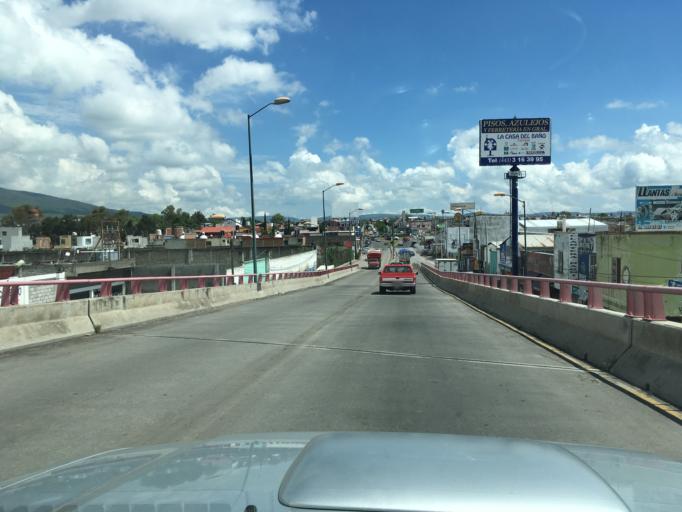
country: MX
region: Michoacan
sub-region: Tarimbaro
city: Real Hacienda (Metropolis)
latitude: 19.7265
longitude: -101.1975
